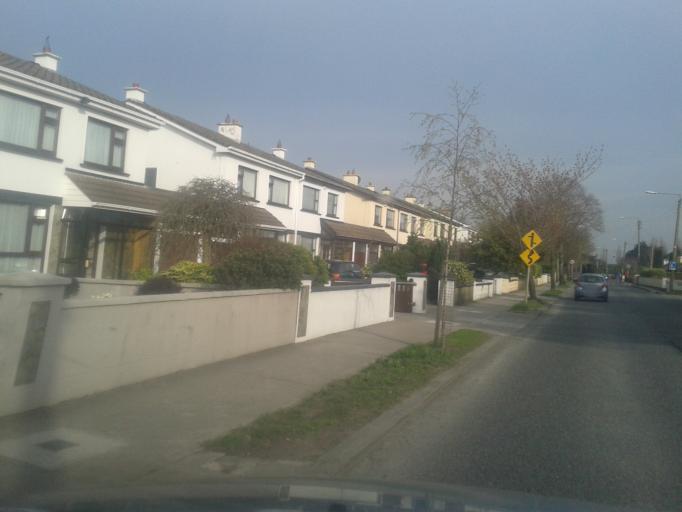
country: IE
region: Leinster
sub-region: Fingal County
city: Swords
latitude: 53.4521
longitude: -6.2112
